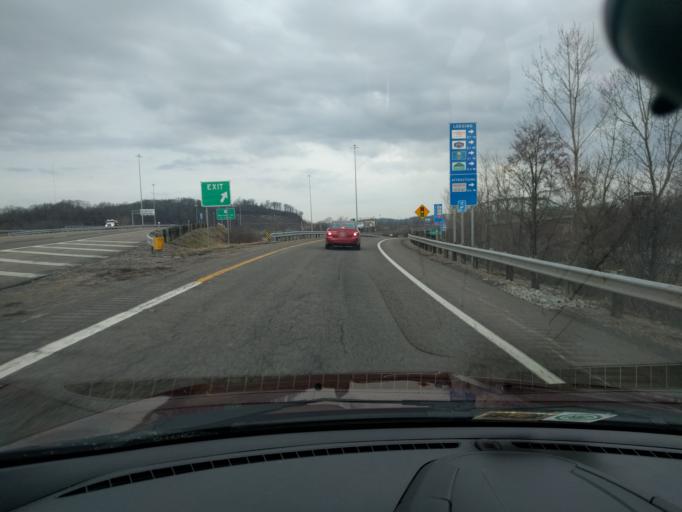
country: US
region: West Virginia
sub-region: Wood County
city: Parkersburg
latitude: 39.2578
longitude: -81.5531
